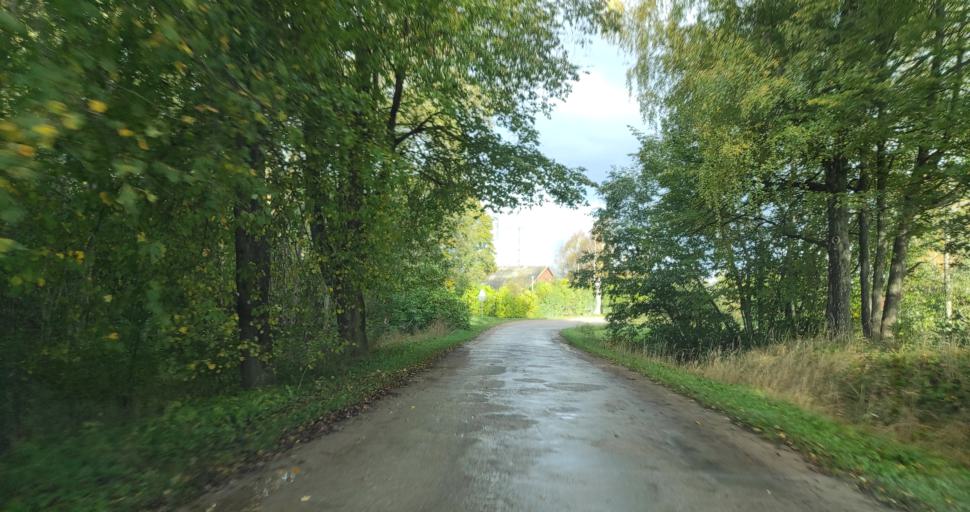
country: LV
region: Aizpute
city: Aizpute
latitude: 56.8028
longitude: 21.6649
